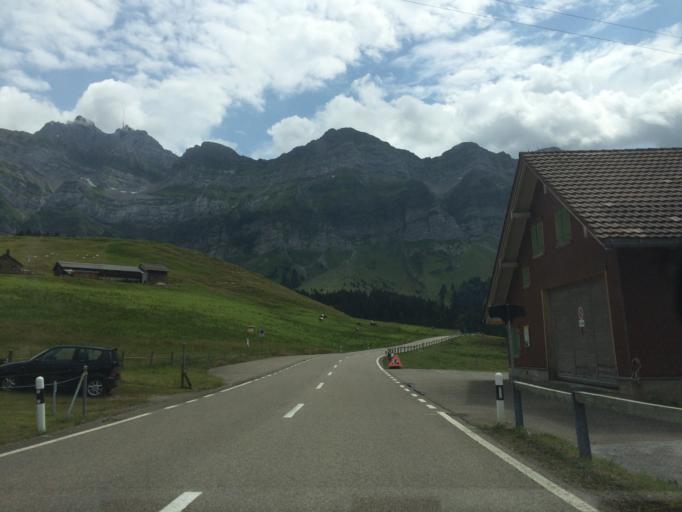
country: CH
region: Appenzell Ausserrhoden
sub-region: Bezirk Hinterland
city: Urnasch
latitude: 47.2642
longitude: 9.3034
